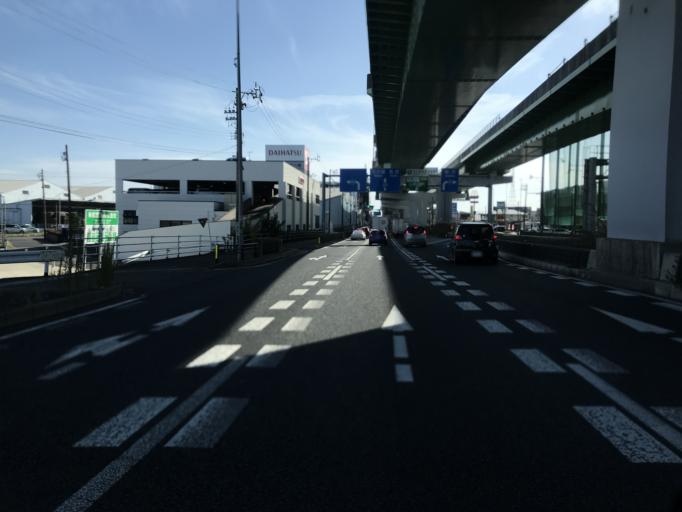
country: JP
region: Aichi
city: Iwakura
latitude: 35.2583
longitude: 136.8424
